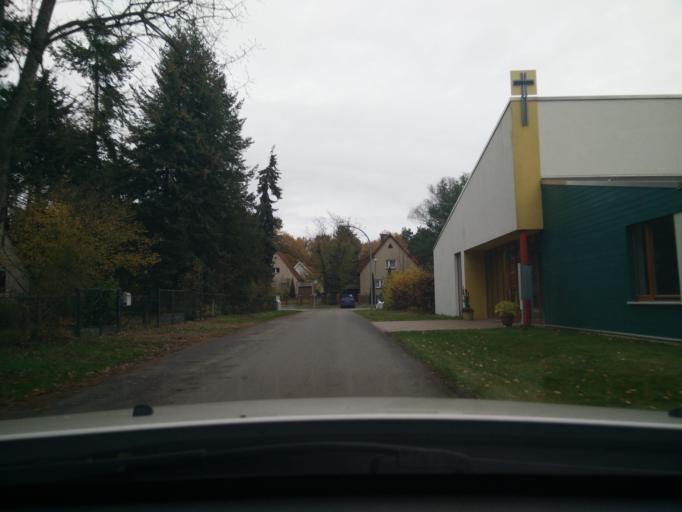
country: DE
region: Berlin
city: Staaken
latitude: 52.5736
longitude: 13.1322
